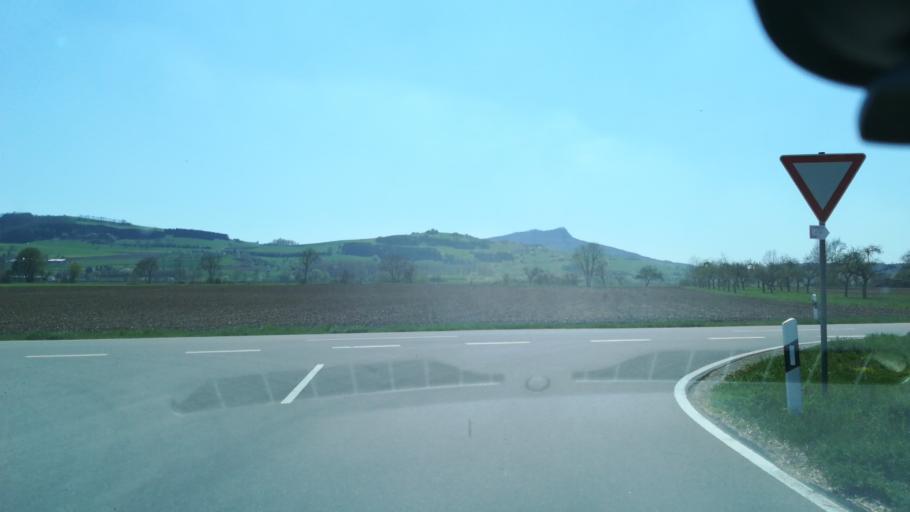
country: DE
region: Baden-Wuerttemberg
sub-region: Freiburg Region
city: Neuhausen
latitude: 47.8299
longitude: 8.7910
